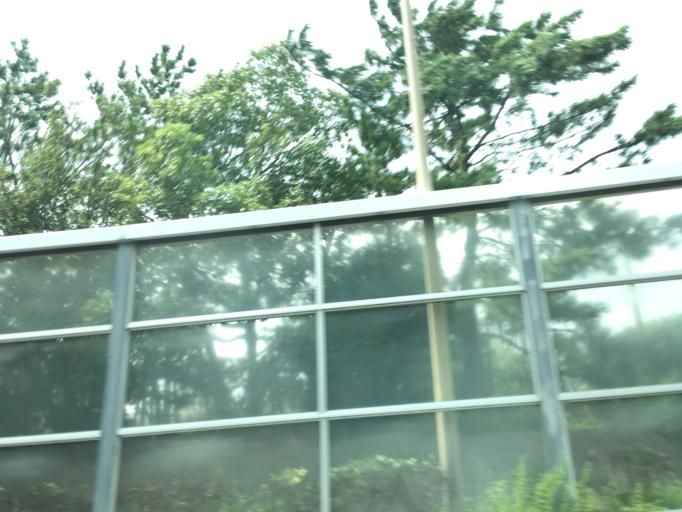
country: JP
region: Hyogo
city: Nishinomiya-hama
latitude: 34.7182
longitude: 135.3209
